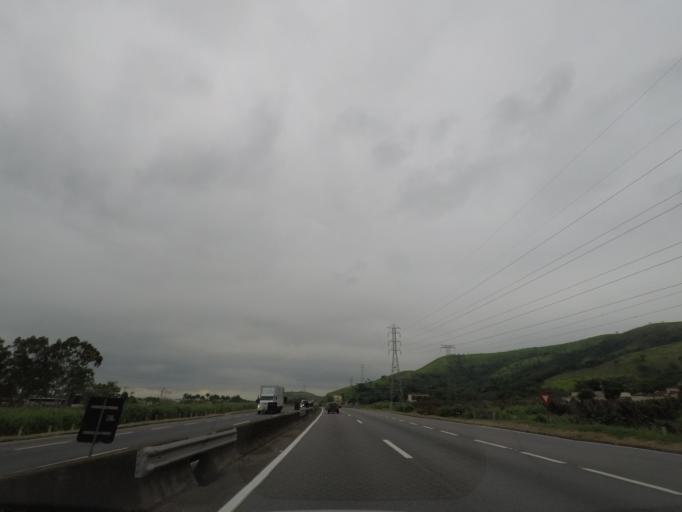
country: BR
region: Sao Paulo
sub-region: Aparecida
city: Aparecida
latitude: -22.8861
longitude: -45.2830
